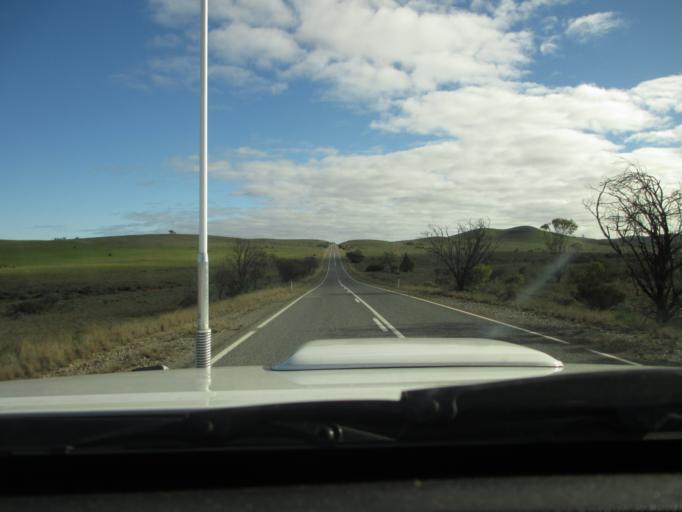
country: AU
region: South Australia
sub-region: Peterborough
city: Peterborough
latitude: -32.6195
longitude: 138.5777
